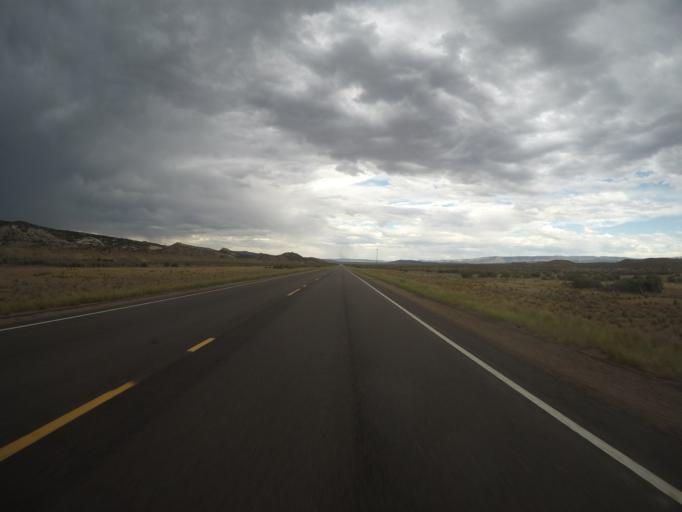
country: US
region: Colorado
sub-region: Rio Blanco County
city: Rangely
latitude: 40.2504
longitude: -108.7747
